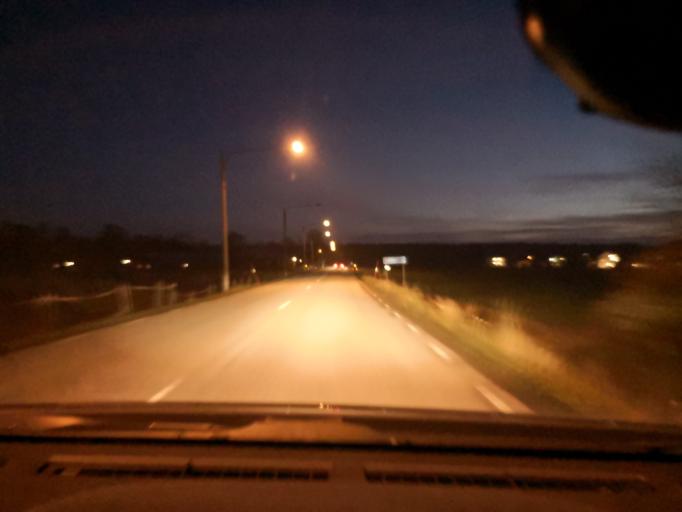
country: SE
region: OErebro
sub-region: Orebro Kommun
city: Orebro
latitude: 59.2595
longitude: 15.2729
